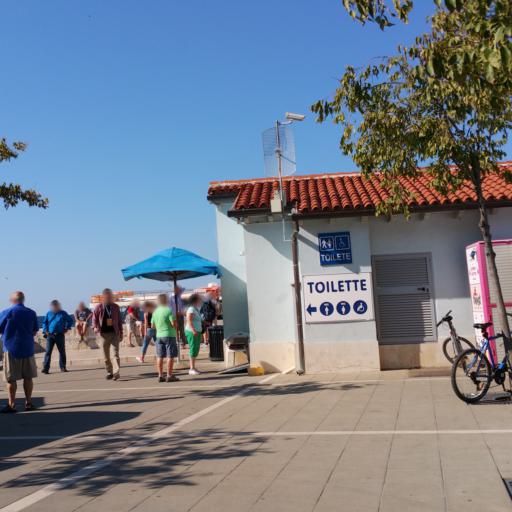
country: HR
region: Istarska
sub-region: Grad Rovinj
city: Rovinj
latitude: 45.0836
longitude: 13.6335
